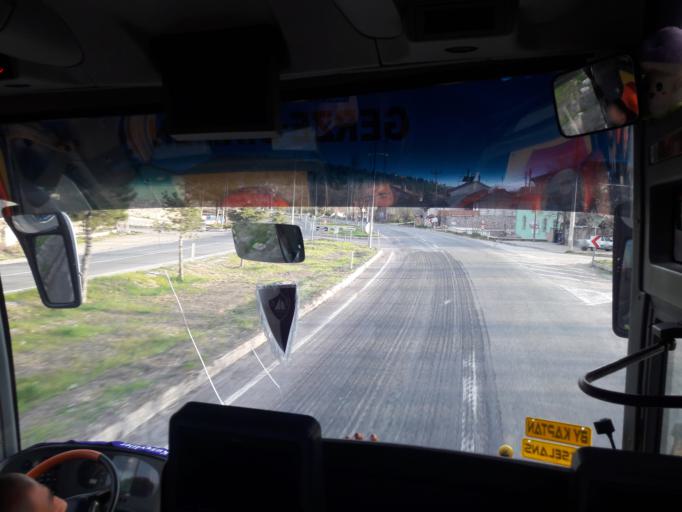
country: TR
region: Cankiri
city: Korgun
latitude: 40.7367
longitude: 33.5198
